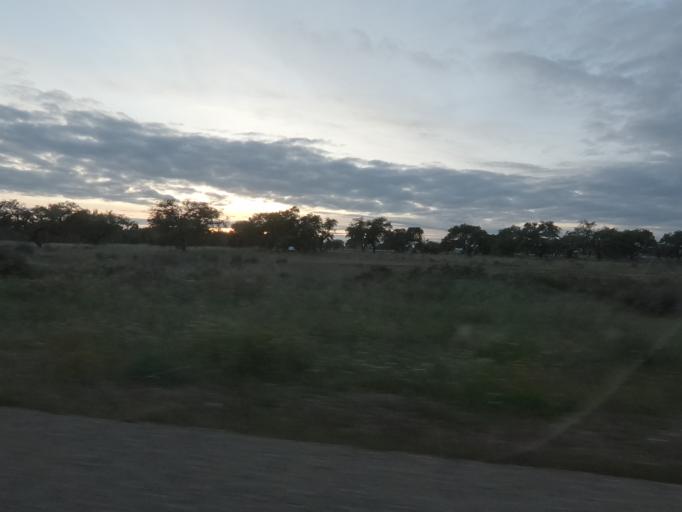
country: ES
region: Extremadura
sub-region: Provincia de Badajoz
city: Badajoz
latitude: 38.9886
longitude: -6.8768
